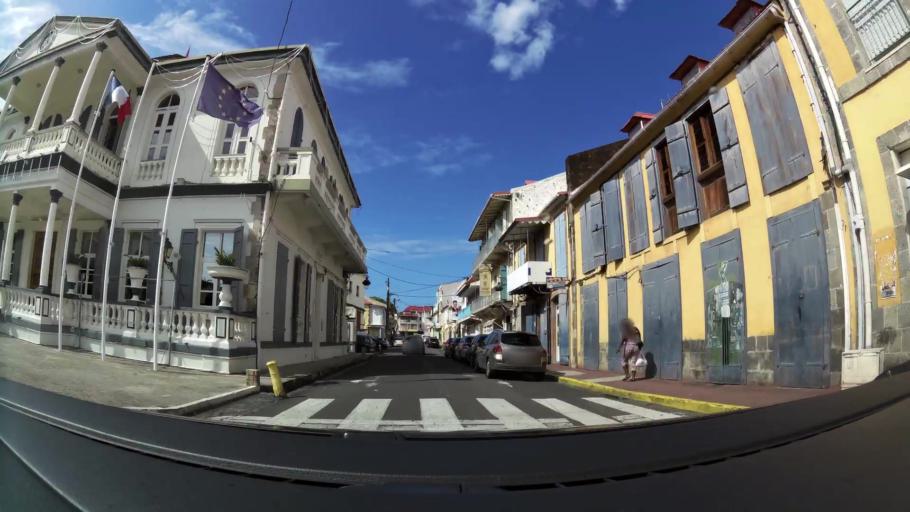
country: GP
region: Guadeloupe
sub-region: Guadeloupe
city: Basse-Terre
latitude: 15.9970
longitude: -61.7321
